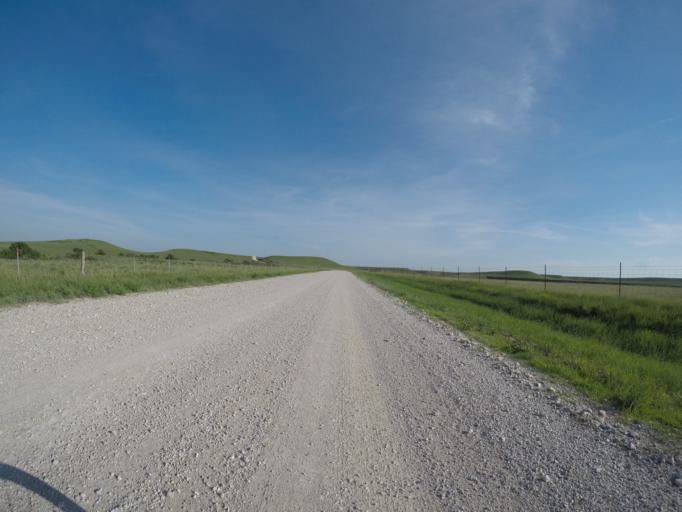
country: US
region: Kansas
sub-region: Riley County
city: Manhattan
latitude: 39.0451
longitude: -96.4935
